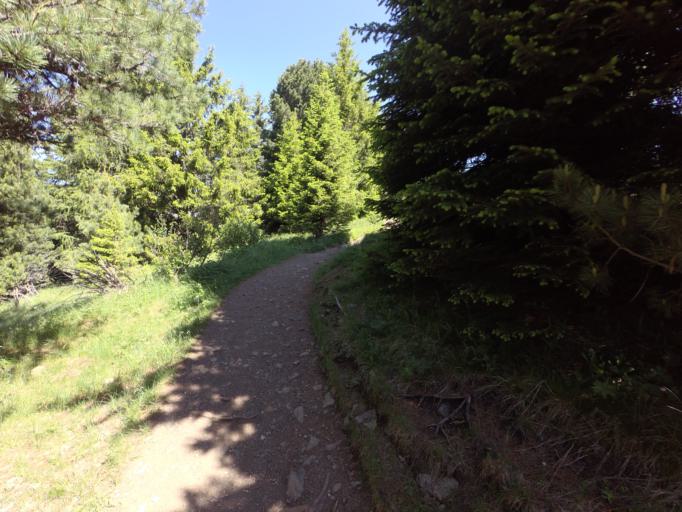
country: IT
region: Trentino-Alto Adige
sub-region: Bolzano
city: Castelrotto
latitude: 46.5560
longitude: 11.5991
